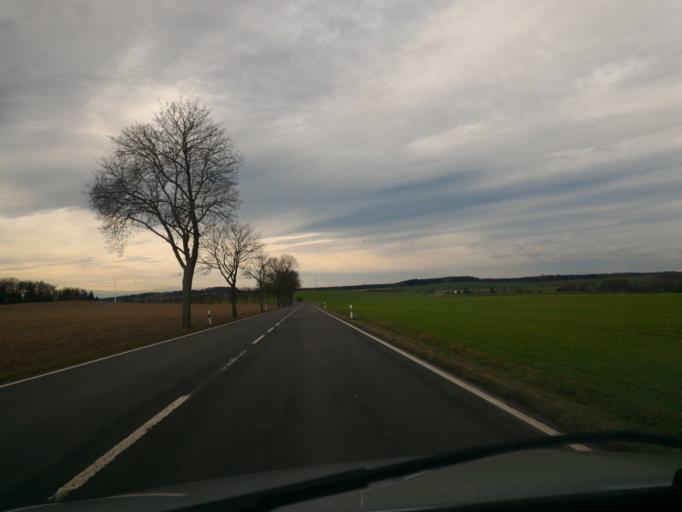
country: DE
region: Saxony
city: Frankenthal
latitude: 51.1121
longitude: 14.1257
